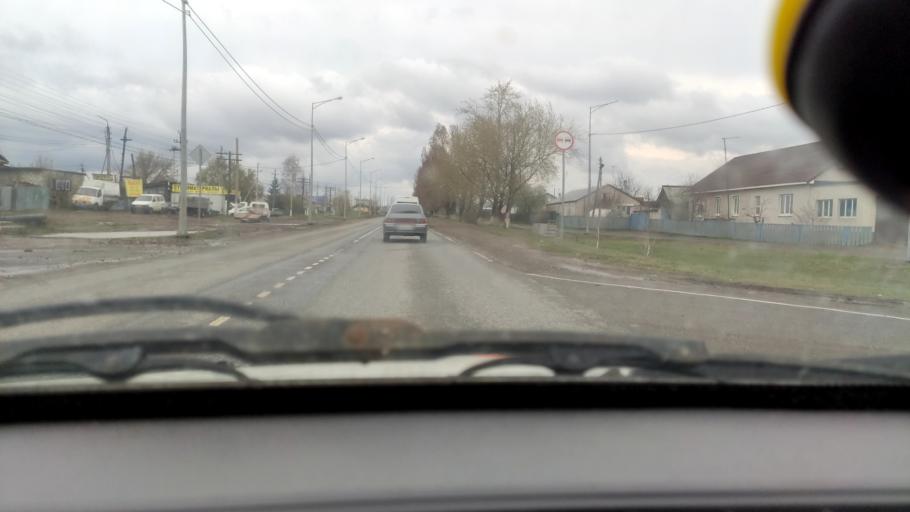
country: RU
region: Samara
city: Zhigulevsk
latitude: 53.5519
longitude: 49.5279
